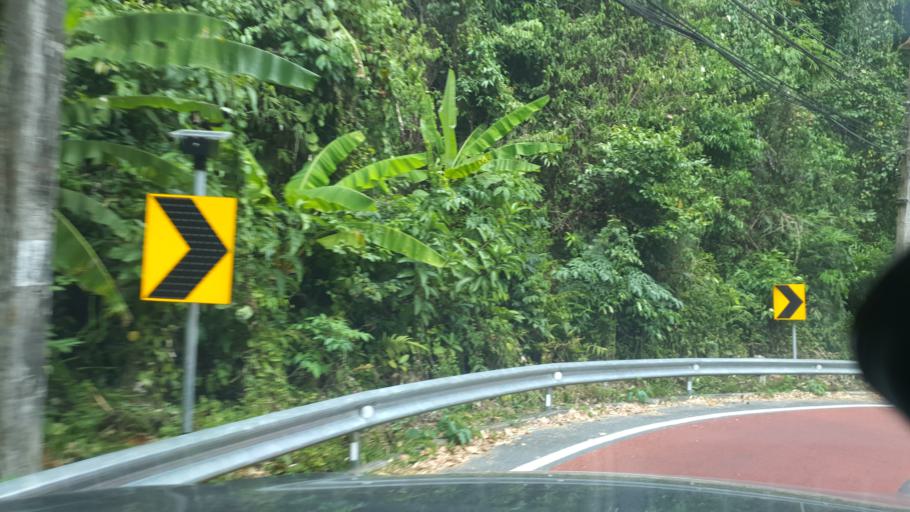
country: TH
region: Phuket
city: Thalang
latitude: 8.0439
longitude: 98.2786
